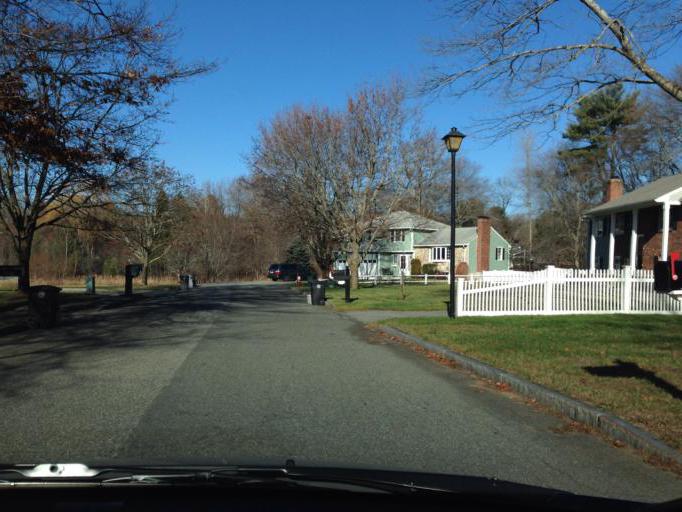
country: US
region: Massachusetts
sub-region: Middlesex County
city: Bedford
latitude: 42.4821
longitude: -71.2820
